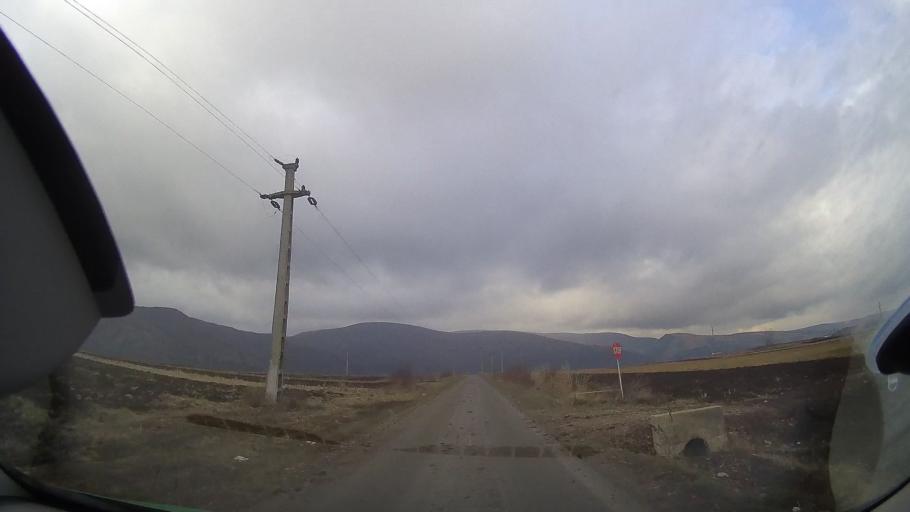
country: RO
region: Cluj
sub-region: Comuna Moldovenesti
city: Moldovenesti
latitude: 46.5021
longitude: 23.6758
